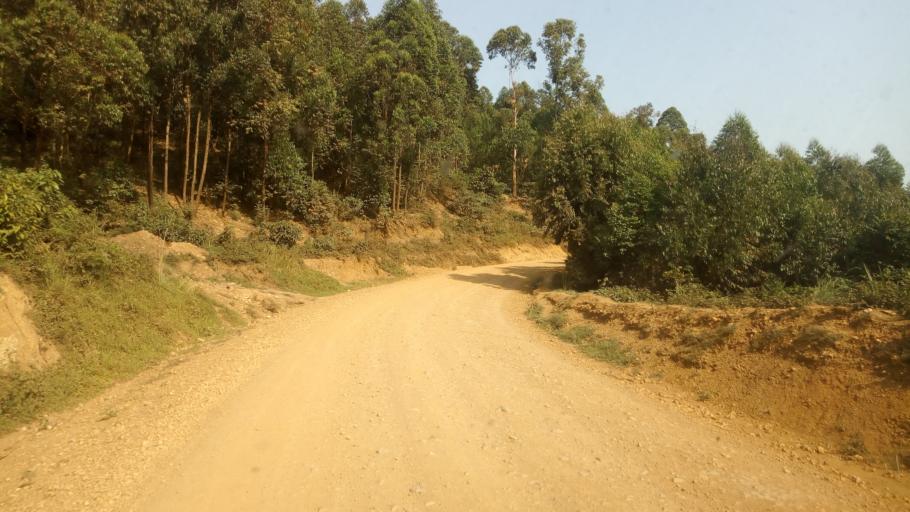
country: UG
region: Western Region
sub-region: Kanungu District
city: Ntungamo
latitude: -0.8316
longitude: 29.6955
